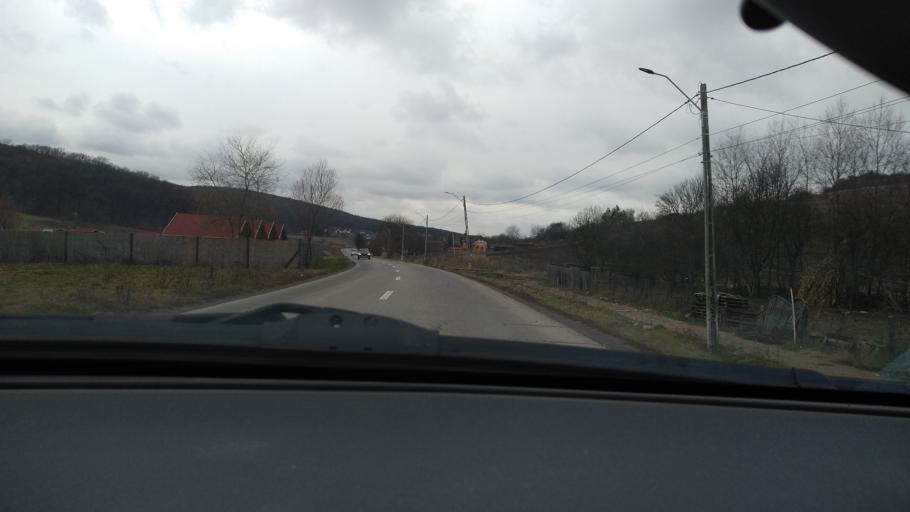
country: RO
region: Mures
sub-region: Comuna Livezeni
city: Livezeni
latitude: 46.5418
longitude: 24.6862
